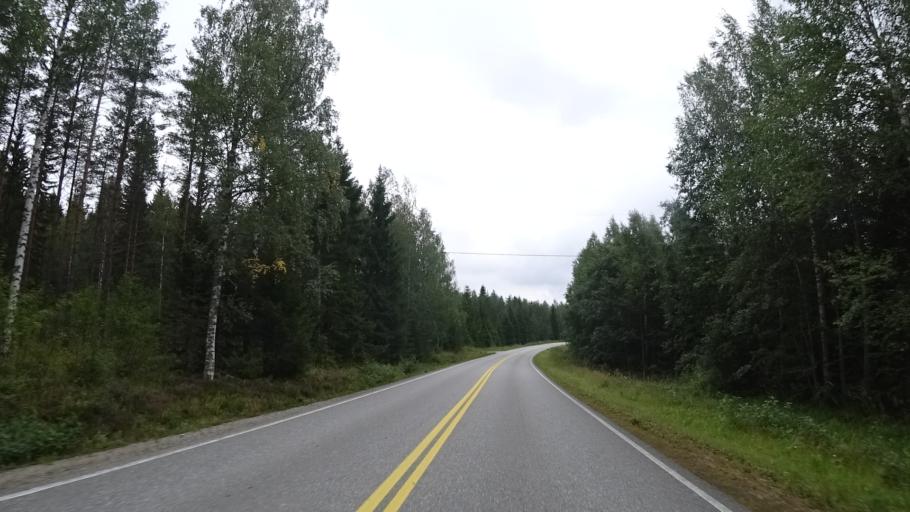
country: FI
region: North Karelia
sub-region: Pielisen Karjala
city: Lieksa
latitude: 63.2816
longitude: 30.5596
